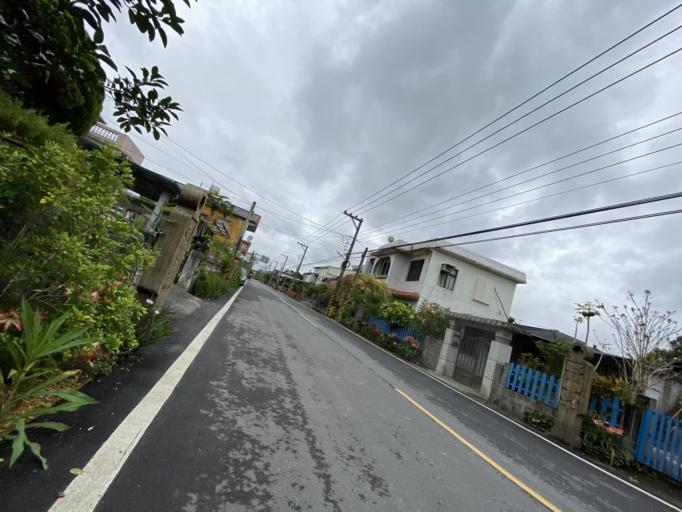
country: TW
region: Taiwan
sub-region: Hualien
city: Hualian
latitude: 23.6573
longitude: 121.4526
